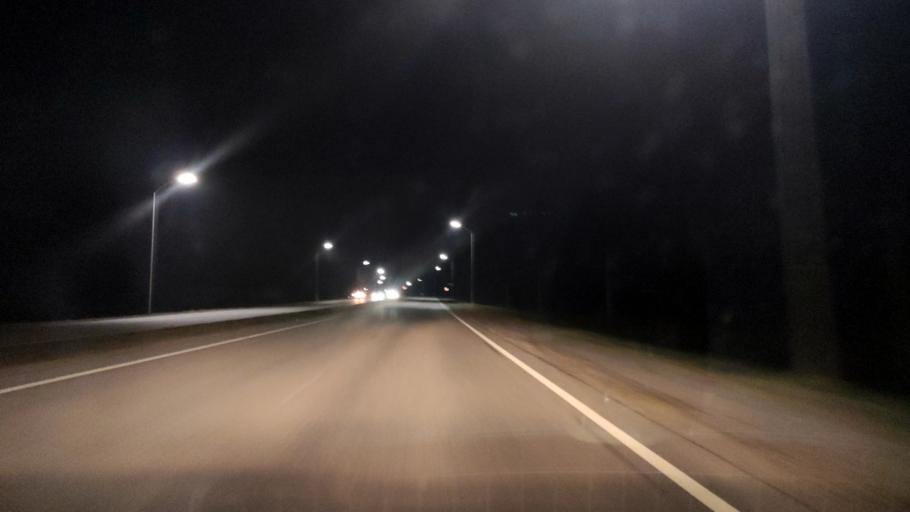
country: RU
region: Belgorod
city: Staryy Oskol
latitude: 51.3923
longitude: 37.8681
